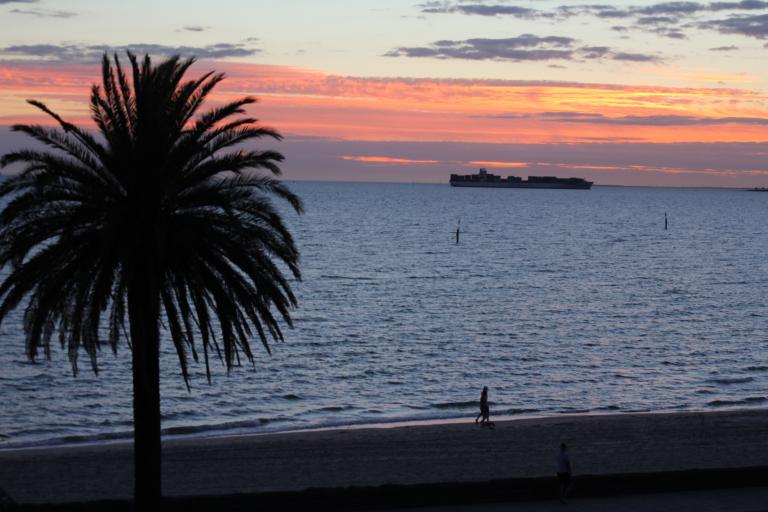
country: AU
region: Victoria
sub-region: Port Phillip
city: Middle Park
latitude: -37.8533
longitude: 144.9607
